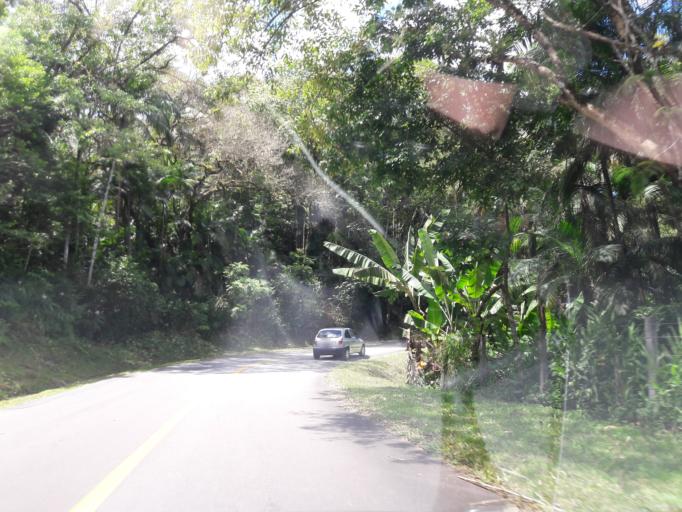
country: BR
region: Parana
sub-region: Antonina
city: Antonina
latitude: -25.4262
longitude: -48.8105
